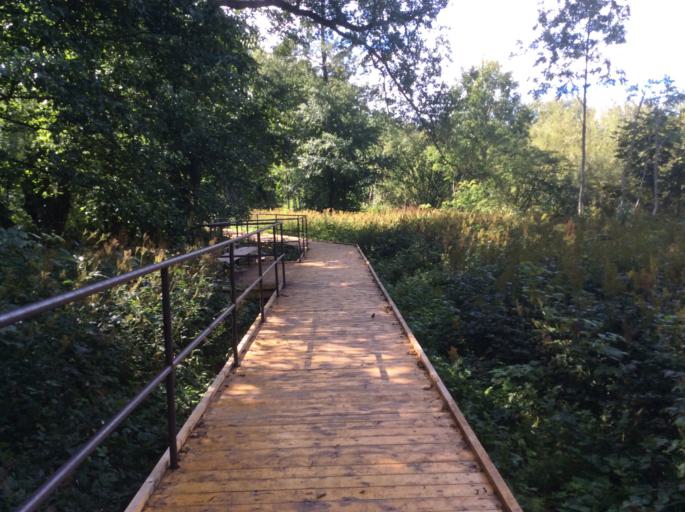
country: SE
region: Gotland
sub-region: Gotland
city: Vibble
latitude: 57.6195
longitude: 18.2703
